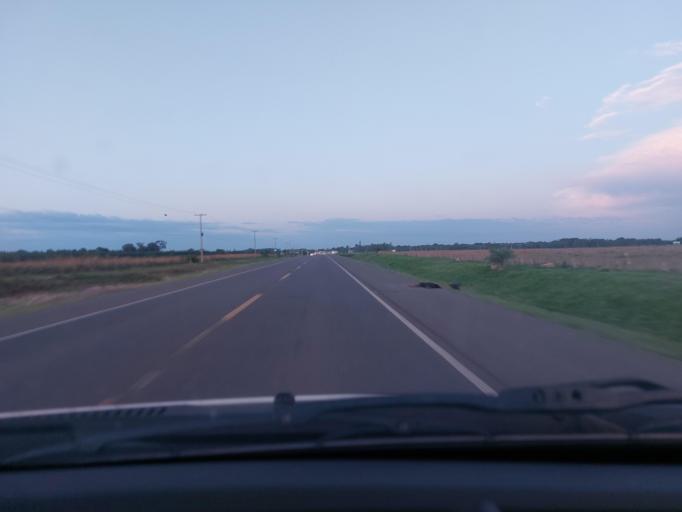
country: PY
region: San Pedro
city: Union
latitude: -24.6912
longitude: -56.4834
